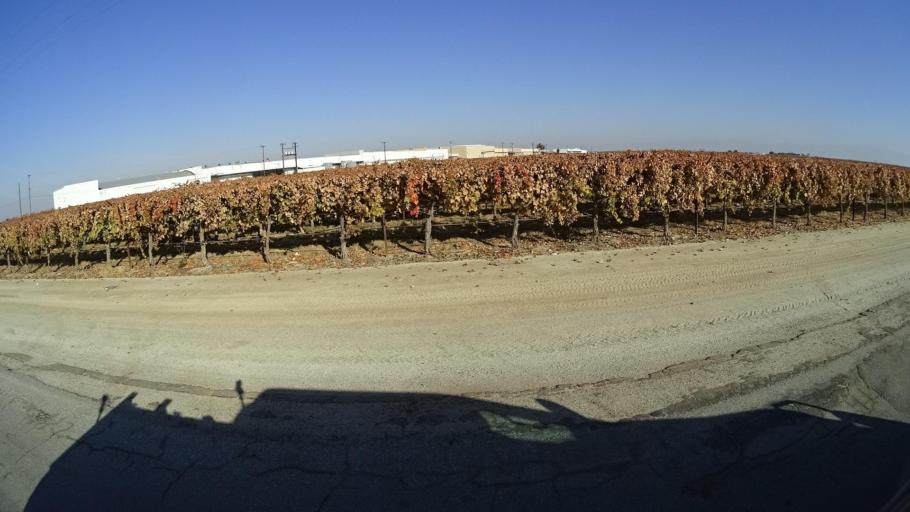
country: US
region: California
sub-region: Tulare County
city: Richgrove
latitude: 35.7398
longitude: -119.1448
